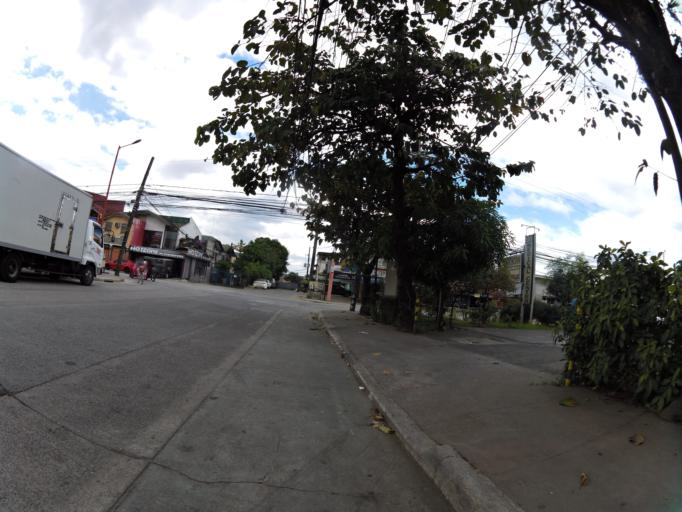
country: PH
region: Calabarzon
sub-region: Province of Rizal
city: Antipolo
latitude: 14.6392
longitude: 121.1099
